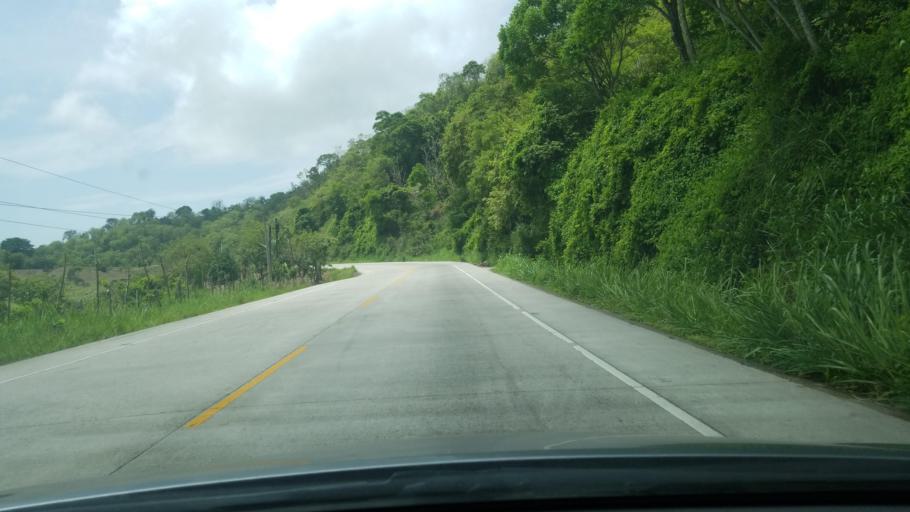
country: HN
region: Copan
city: Veracruz
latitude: 14.9201
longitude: -88.7623
